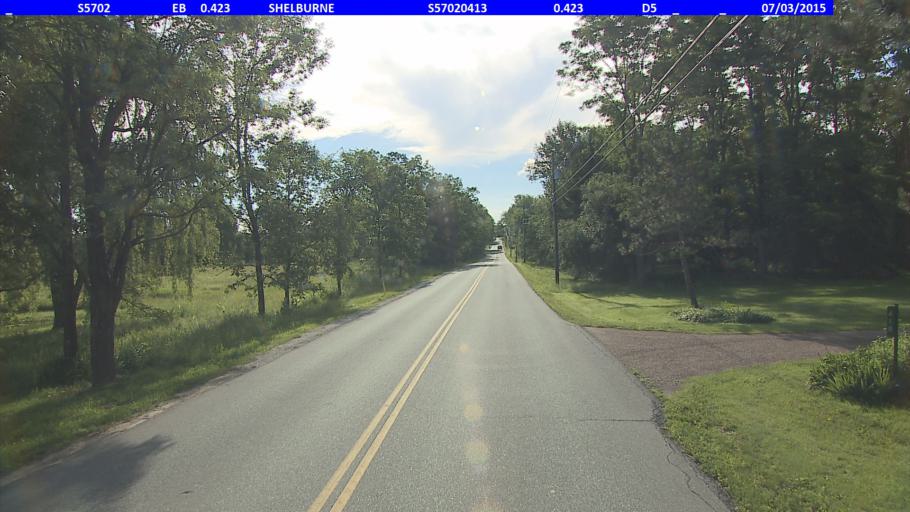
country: US
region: Vermont
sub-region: Chittenden County
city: South Burlington
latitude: 44.4087
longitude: -73.1895
